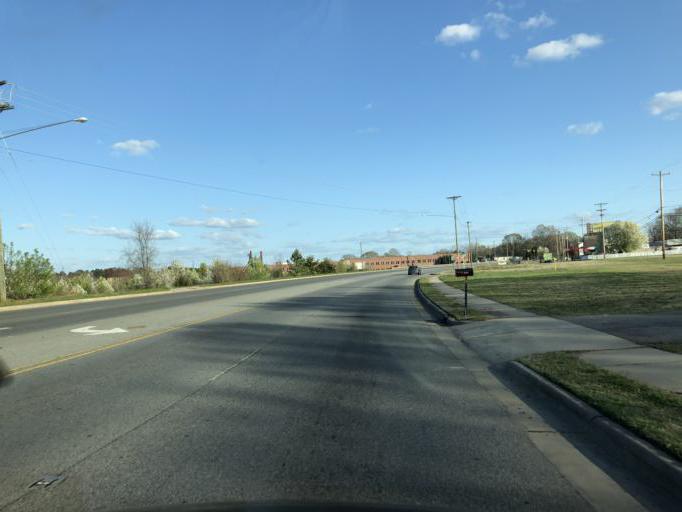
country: US
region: North Carolina
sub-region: Gaston County
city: Gastonia
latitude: 35.2733
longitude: -81.2248
